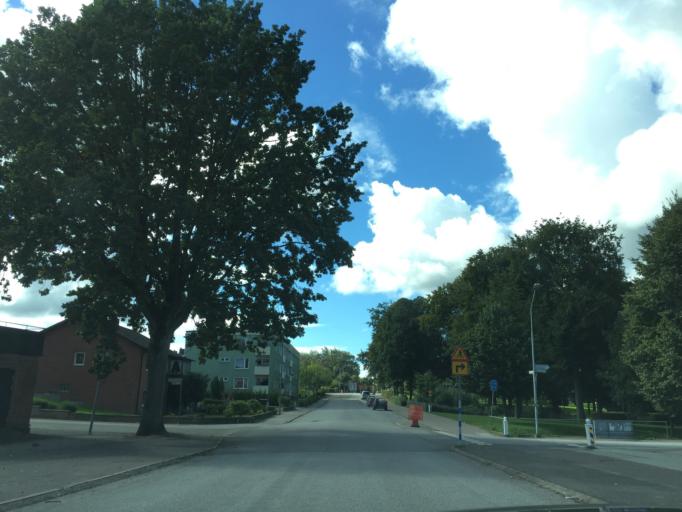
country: SE
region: Skane
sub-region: Sjobo Kommun
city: Sjoebo
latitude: 55.6336
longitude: 13.7030
